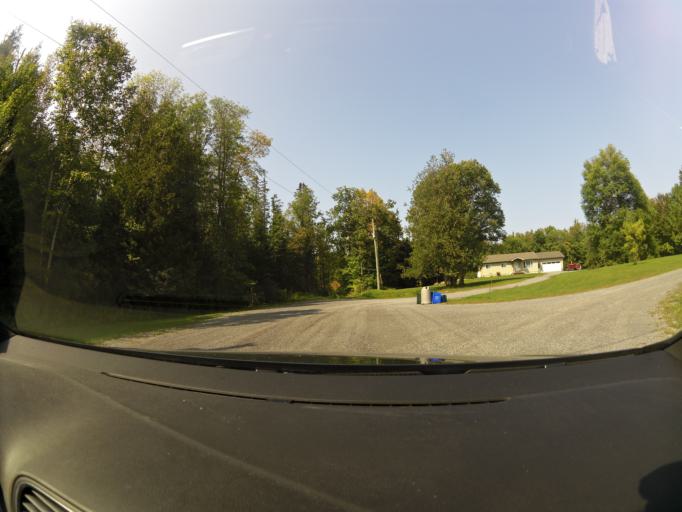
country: CA
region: Ontario
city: Arnprior
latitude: 45.4517
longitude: -76.1706
